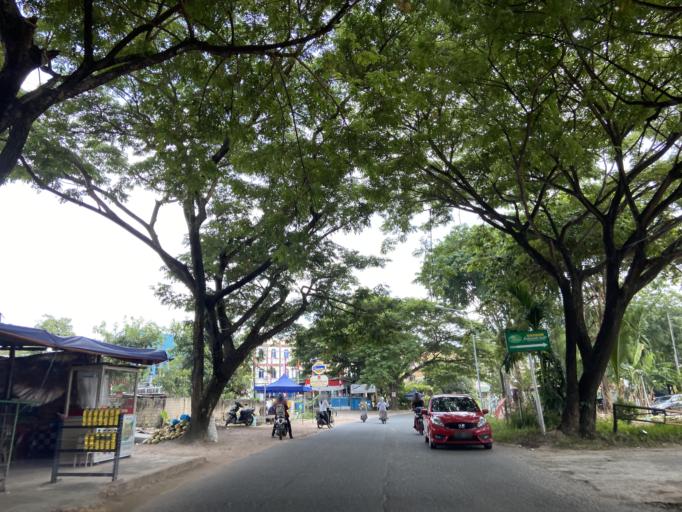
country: SG
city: Singapore
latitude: 1.1322
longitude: 104.0340
